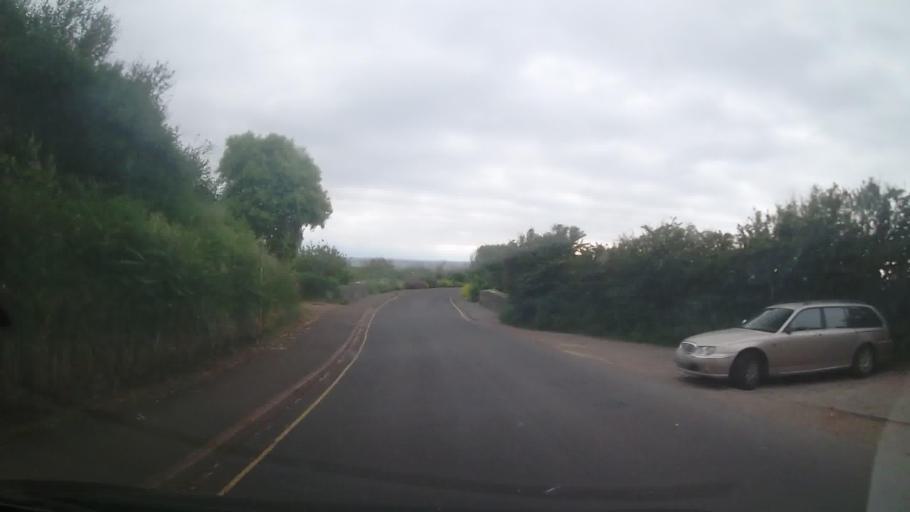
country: GB
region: England
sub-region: Devon
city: Dartmouth
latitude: 50.2875
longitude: -3.6473
